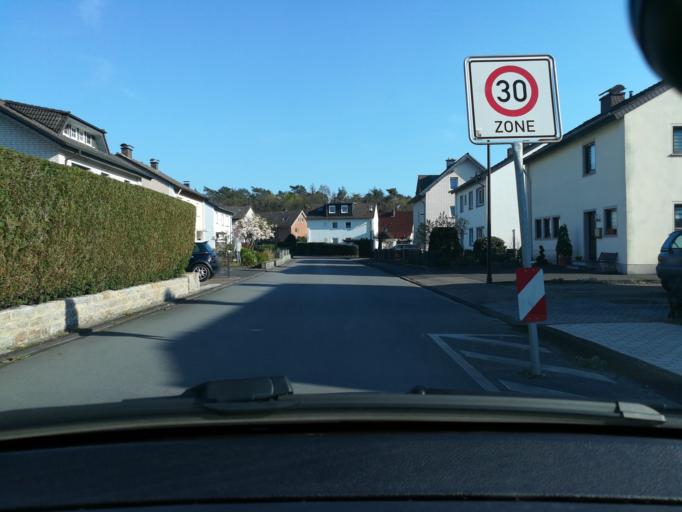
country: DE
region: North Rhine-Westphalia
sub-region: Regierungsbezirk Detmold
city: Verl
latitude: 51.9150
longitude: 8.5892
